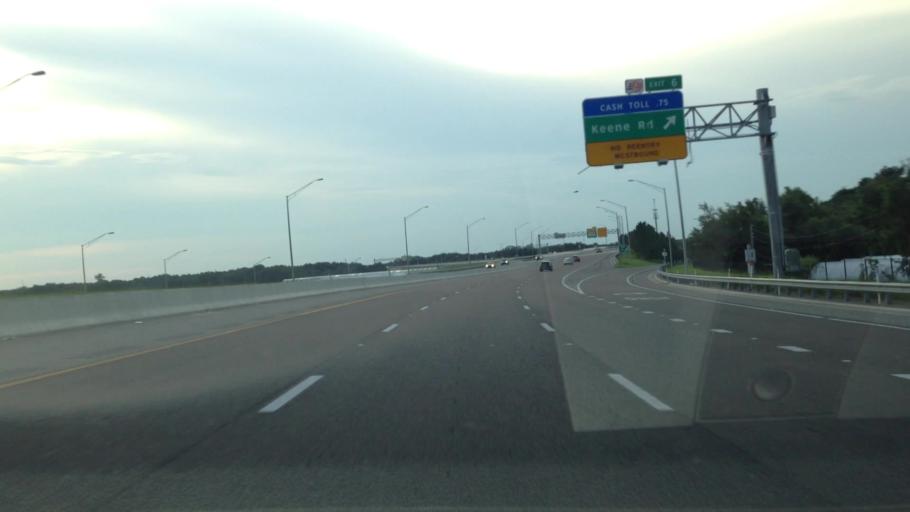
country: US
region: Florida
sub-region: Orange County
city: Clarcona
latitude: 28.6362
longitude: -81.4932
